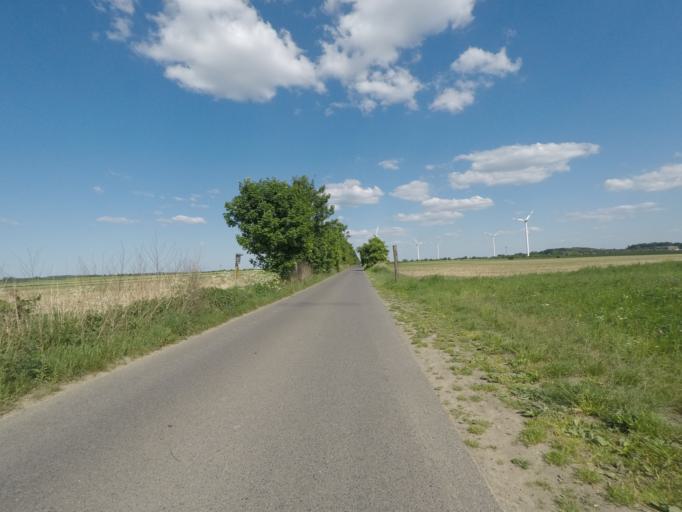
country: DE
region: Brandenburg
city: Britz
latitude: 52.8787
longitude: 13.7534
